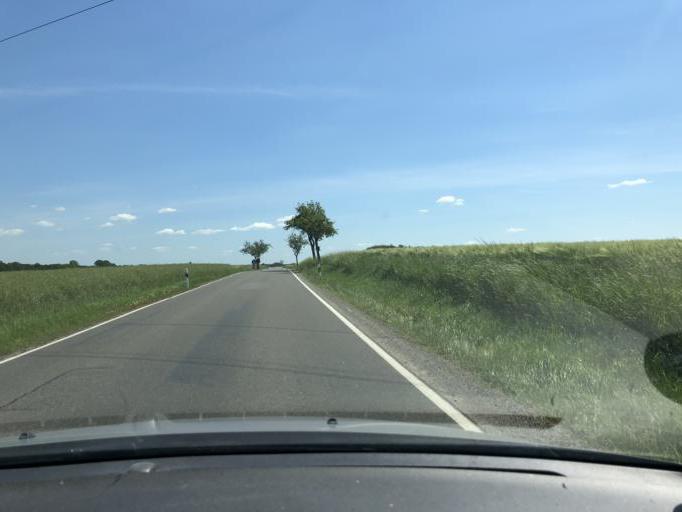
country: DE
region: Saxony
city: Trebsen
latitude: 51.2895
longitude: 12.7061
